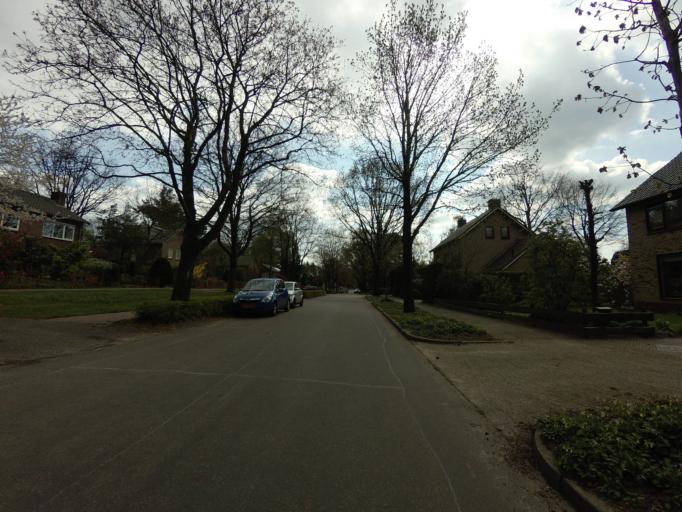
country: NL
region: Utrecht
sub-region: Gemeente Utrechtse Heuvelrug
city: Doorn
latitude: 52.0471
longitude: 5.3363
